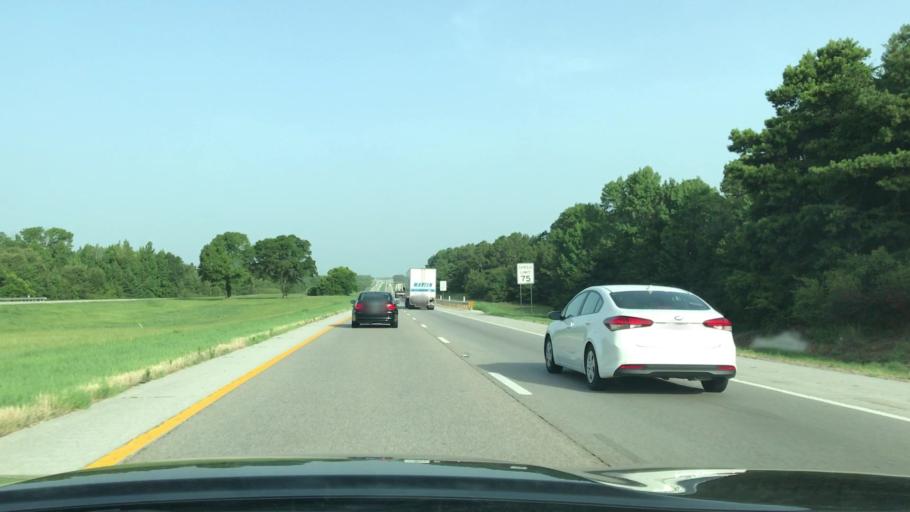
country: US
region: Texas
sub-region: Smith County
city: Hideaway
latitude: 32.4849
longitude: -95.5309
